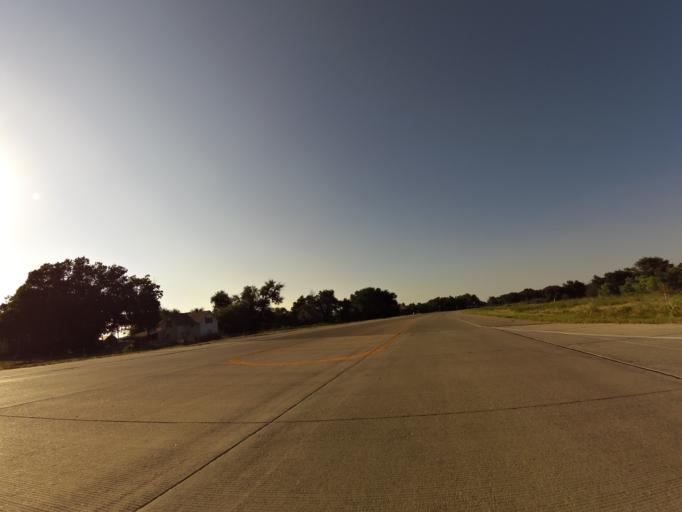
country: US
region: Kansas
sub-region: Reno County
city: Buhler
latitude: 38.1542
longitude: -97.8485
